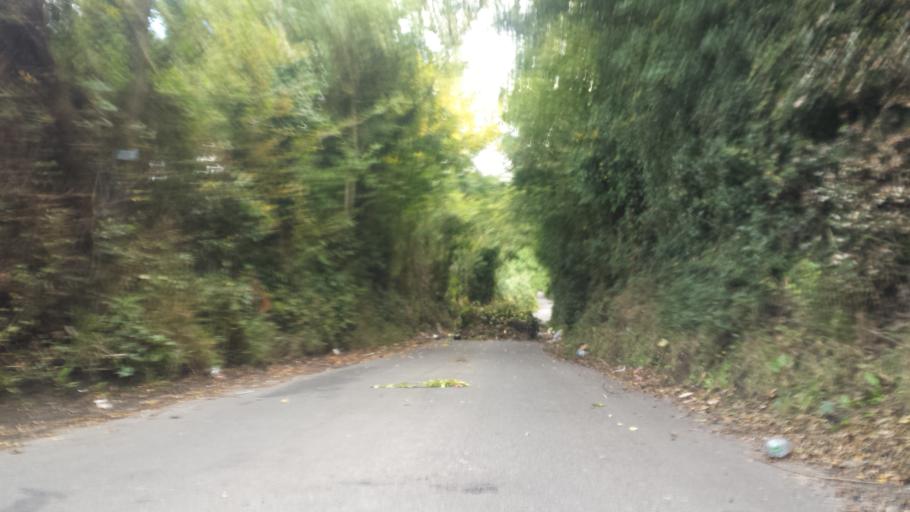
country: GB
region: England
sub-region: Greater London
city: Orpington
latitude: 51.3938
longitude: 0.1290
